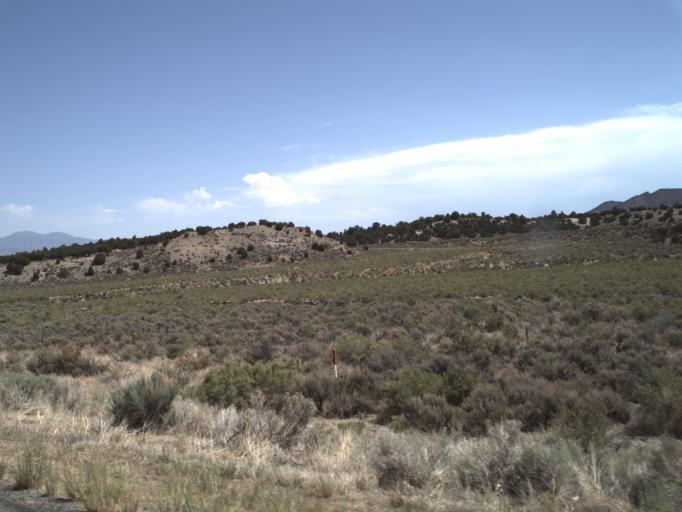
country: US
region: Utah
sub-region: Utah County
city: Eagle Mountain
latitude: 40.0101
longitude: -112.2764
